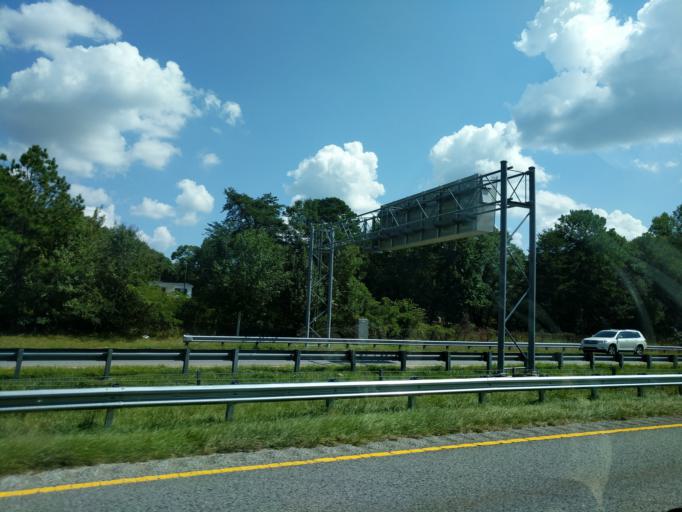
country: US
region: South Carolina
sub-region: Spartanburg County
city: Roebuck
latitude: 34.8961
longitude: -81.9924
